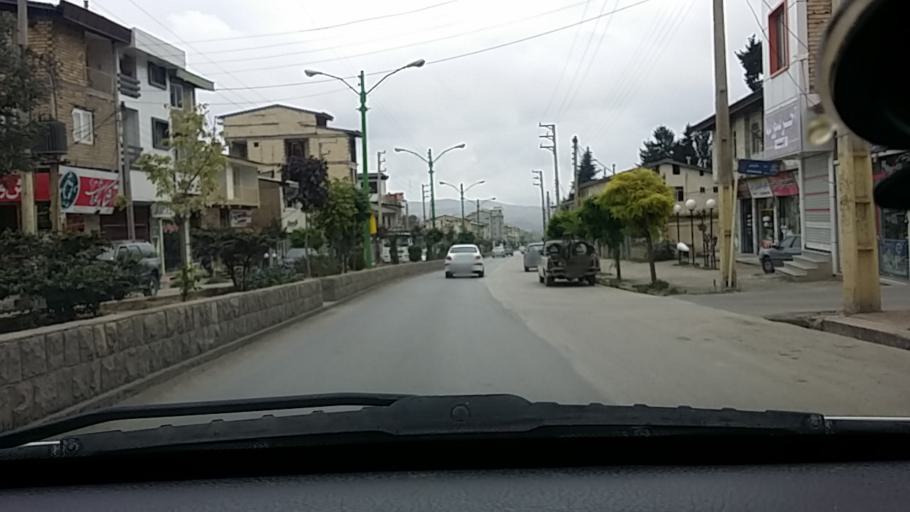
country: IR
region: Mazandaran
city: `Abbasabad
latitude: 36.5074
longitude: 51.1651
